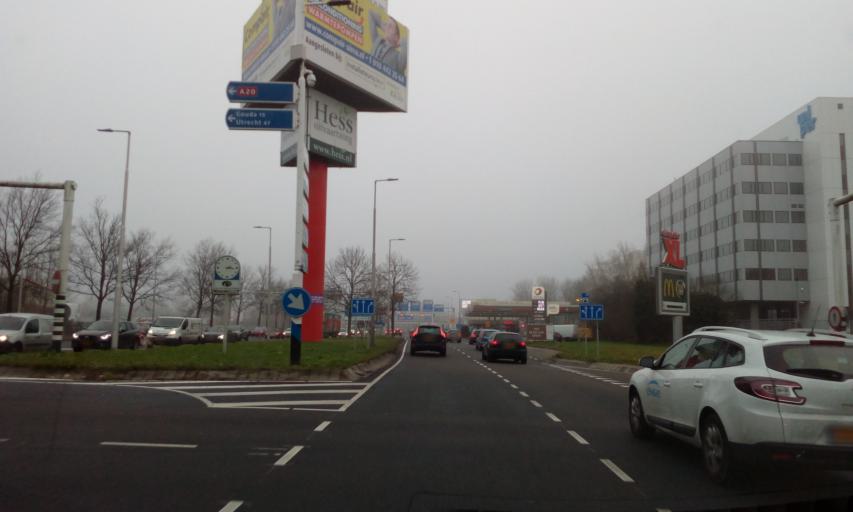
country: NL
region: South Holland
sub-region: Gemeente Capelle aan den IJssel
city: Capelle aan den IJssel
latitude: 51.9553
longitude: 4.5626
